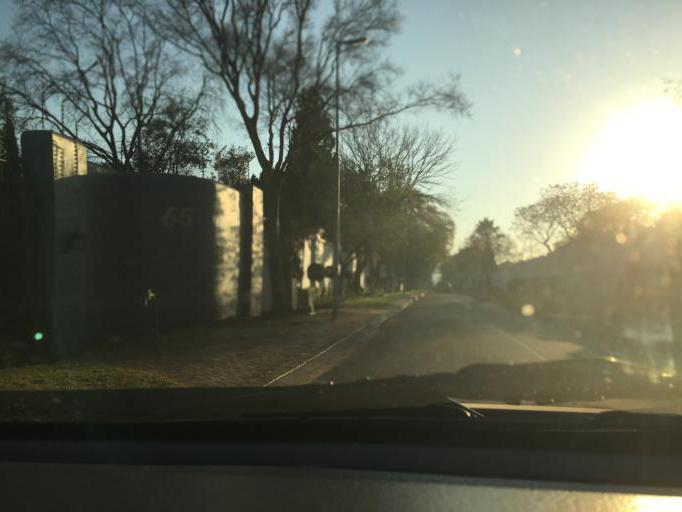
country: ZA
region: Gauteng
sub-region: City of Johannesburg Metropolitan Municipality
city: Diepsloot
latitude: -26.0680
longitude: 28.0029
